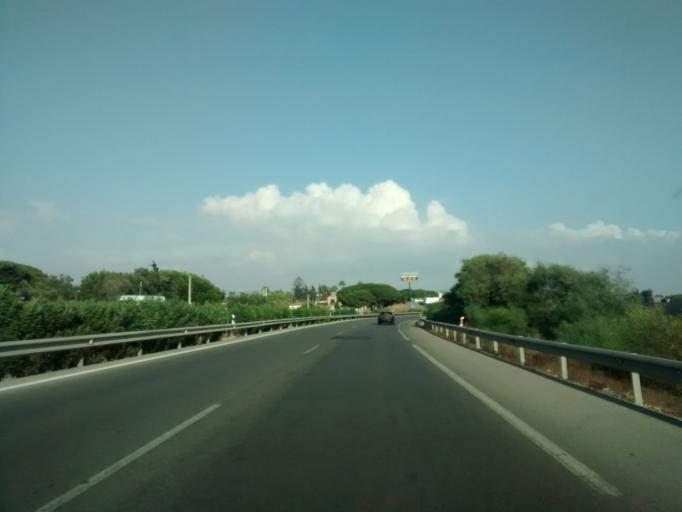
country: ES
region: Andalusia
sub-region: Provincia de Cadiz
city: Chiclana de la Frontera
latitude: 36.4442
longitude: -6.1384
